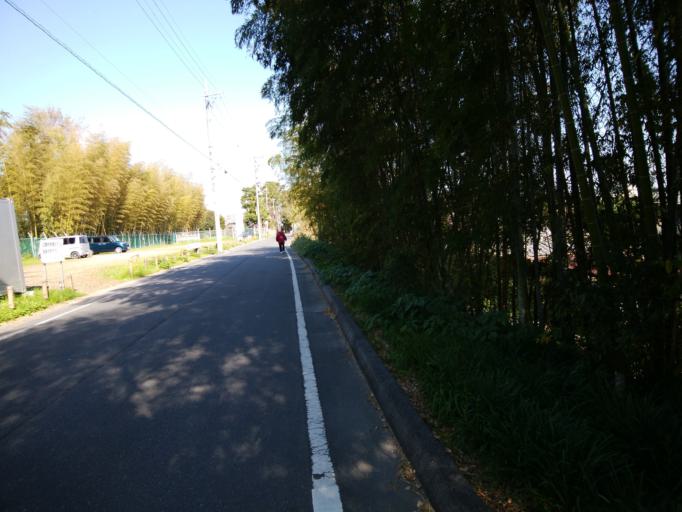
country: JP
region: Aichi
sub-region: Tsushima-shi
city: Tsushima
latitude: 35.1703
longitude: 136.7204
